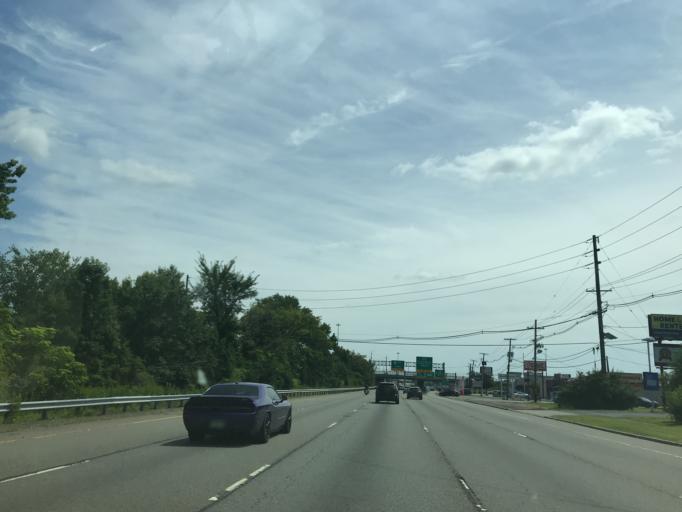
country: US
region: New Jersey
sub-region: Passaic County
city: Singac
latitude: 40.8947
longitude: -74.2407
